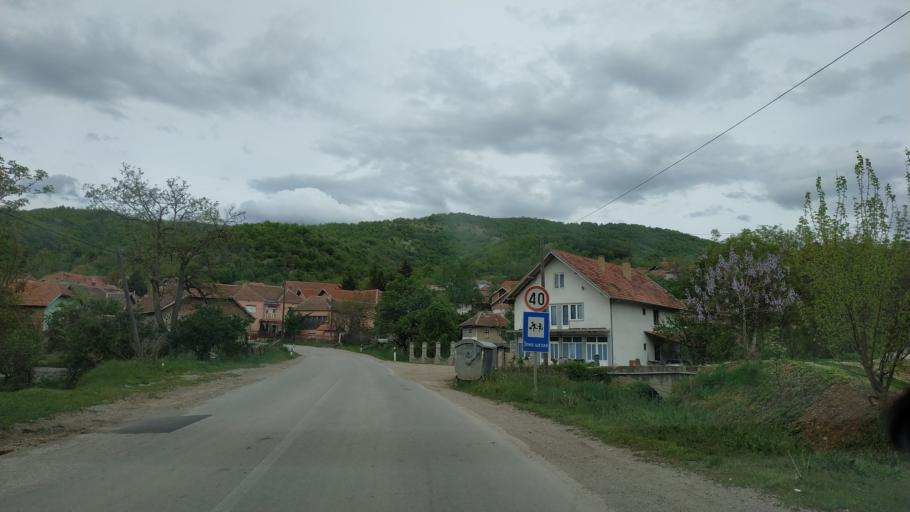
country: RS
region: Central Serbia
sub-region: Nisavski Okrug
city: Aleksinac
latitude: 43.6330
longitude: 21.7176
